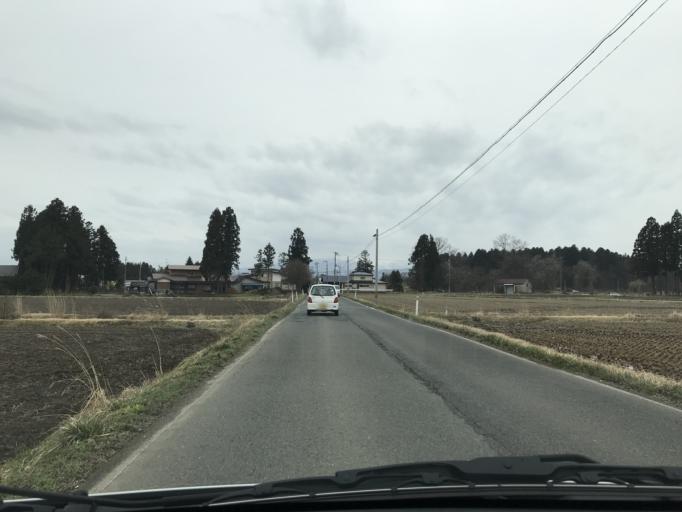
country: JP
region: Iwate
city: Kitakami
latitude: 39.3214
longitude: 141.0699
